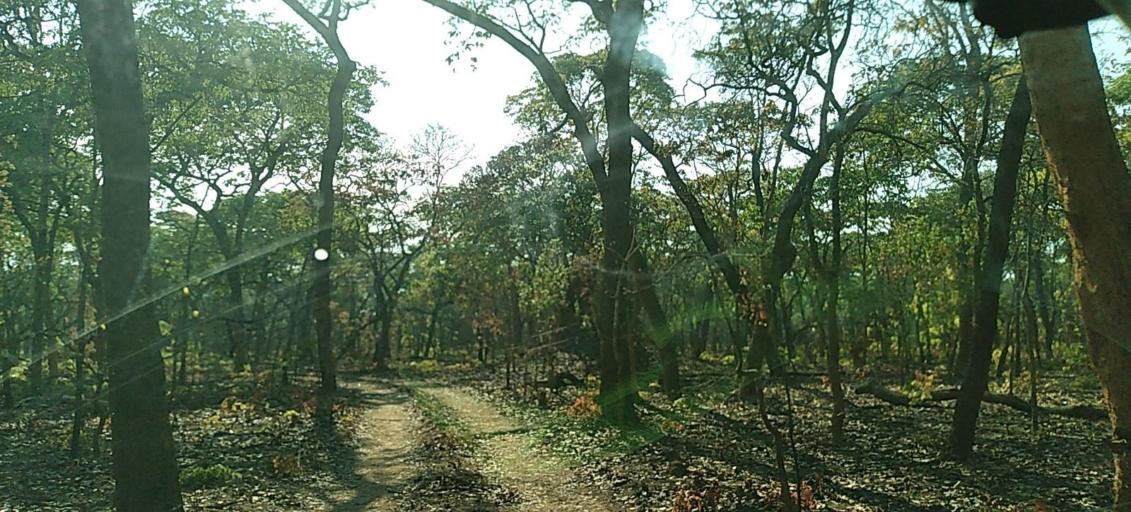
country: ZM
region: North-Western
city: Kalengwa
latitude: -13.2337
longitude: 25.0709
